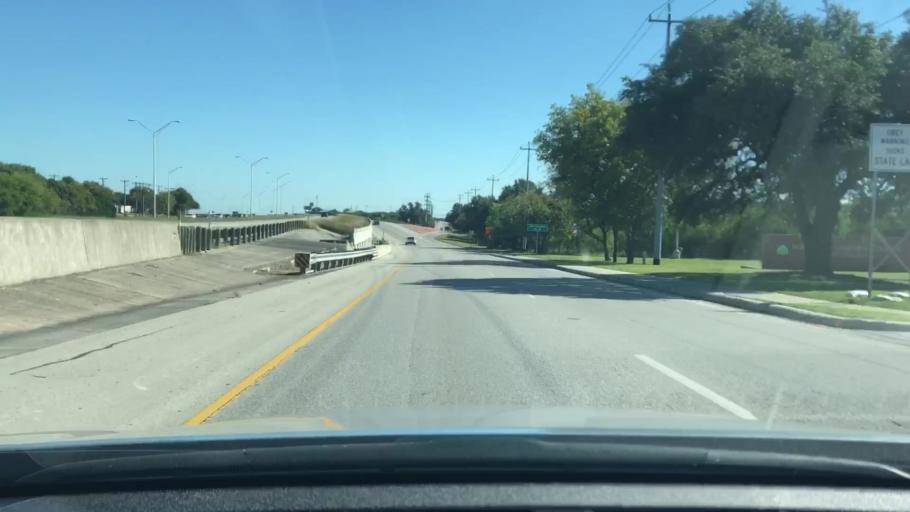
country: US
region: Texas
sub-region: Bexar County
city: Live Oak
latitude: 29.5516
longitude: -98.3217
